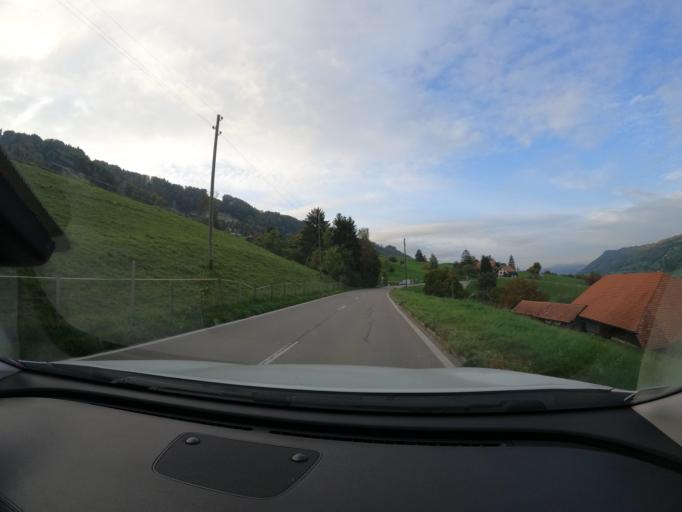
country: CH
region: Bern
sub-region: Bern-Mittelland District
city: Hermiswil
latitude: 46.8385
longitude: 7.4927
